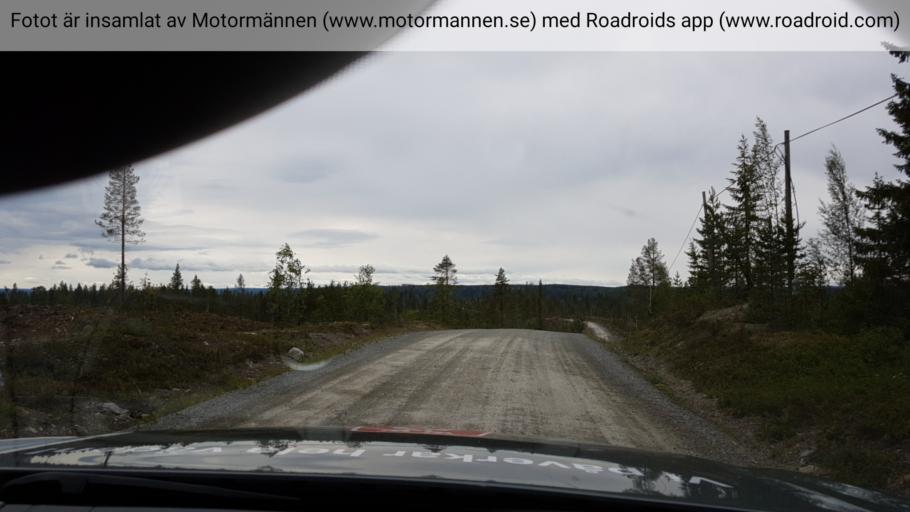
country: SE
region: Jaemtland
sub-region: Are Kommun
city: Jarpen
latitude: 62.8098
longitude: 13.8087
